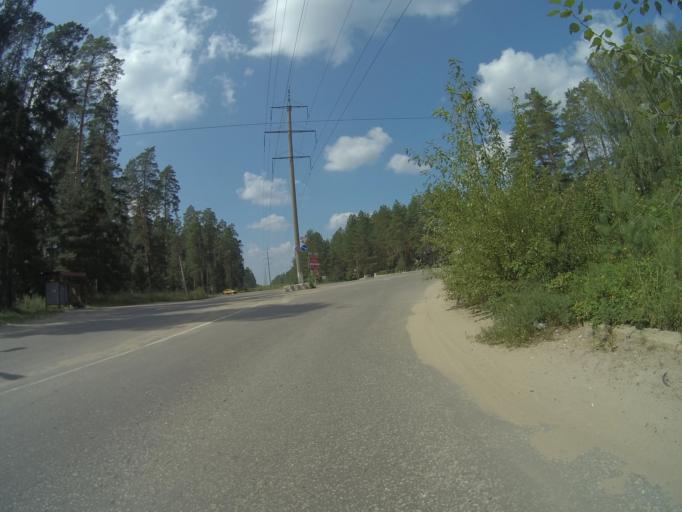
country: RU
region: Vladimir
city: Gus'-Khrustal'nyy
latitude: 55.6323
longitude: 40.6954
